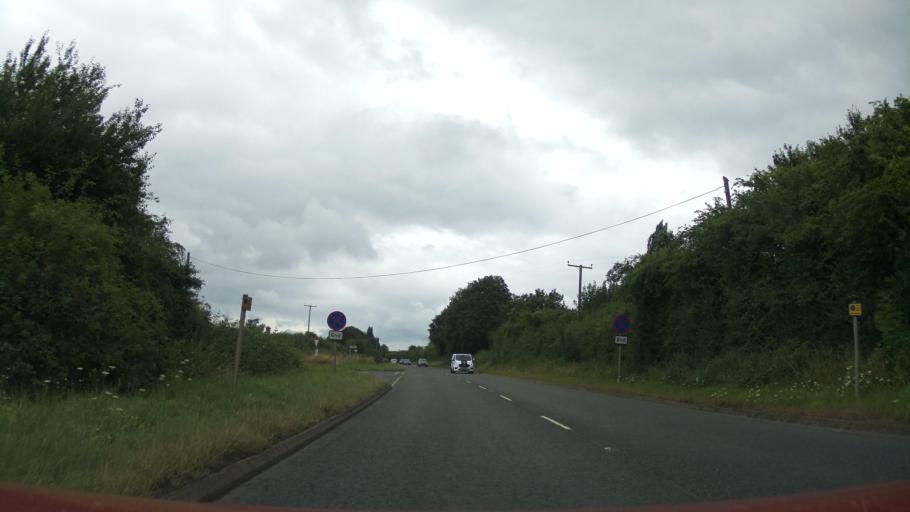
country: GB
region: England
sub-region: Worcestershire
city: Fernhill Heath
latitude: 52.2234
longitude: -2.1649
